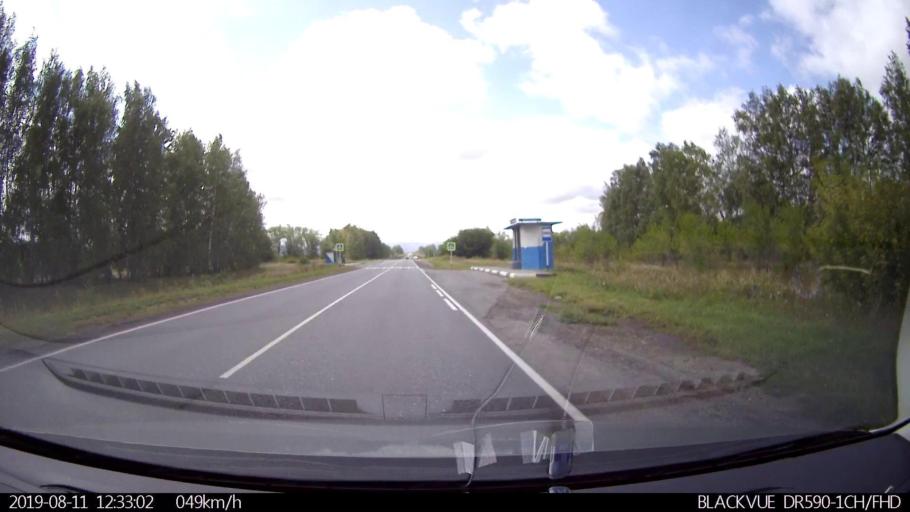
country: RU
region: Ulyanovsk
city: Ignatovka
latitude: 53.8104
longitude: 47.8587
